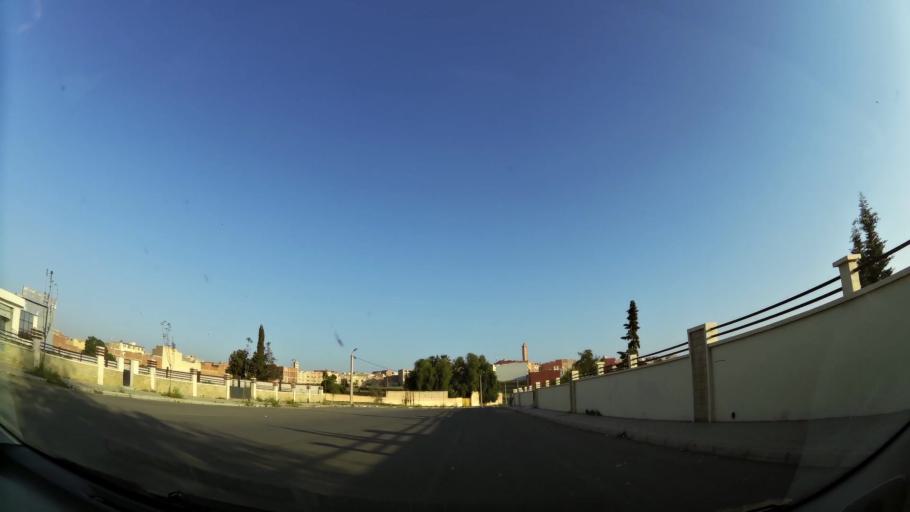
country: MA
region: Oriental
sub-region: Oujda-Angad
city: Oujda
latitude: 34.6721
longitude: -1.9360
